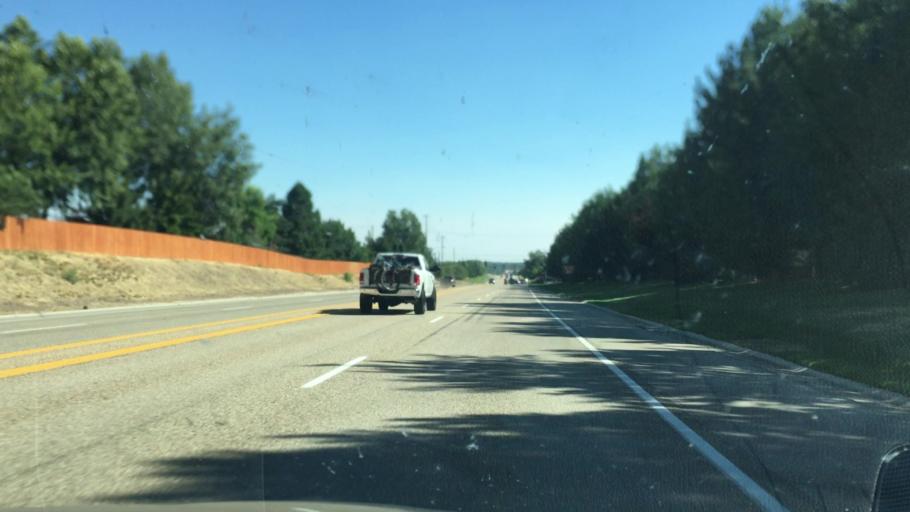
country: US
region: Idaho
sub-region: Ada County
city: Eagle
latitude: 43.7091
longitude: -116.3190
